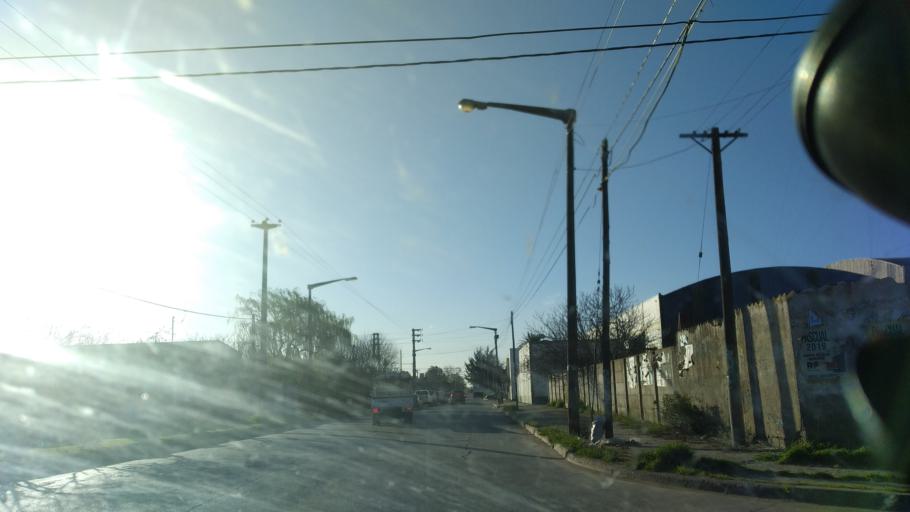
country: AR
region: Buenos Aires
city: Necochea
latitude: -38.5593
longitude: -58.7141
